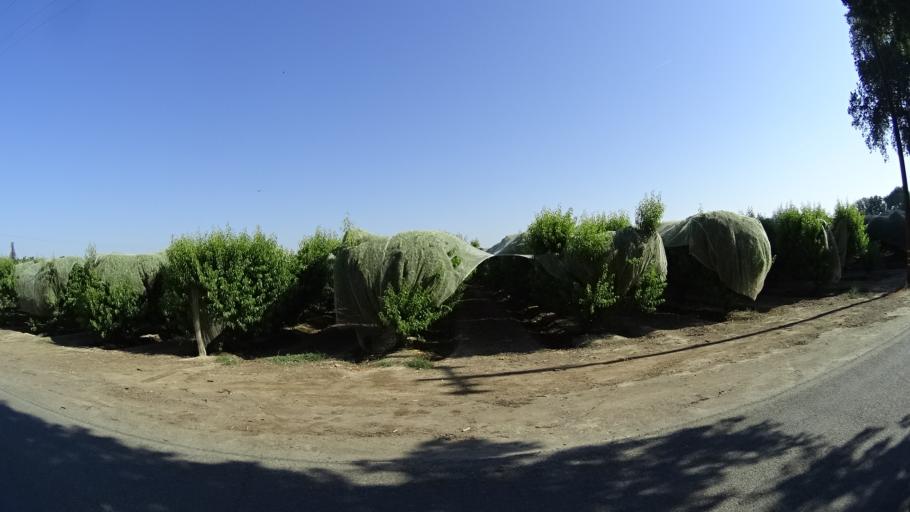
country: US
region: California
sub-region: Kings County
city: Lucerne
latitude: 36.3864
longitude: -119.6541
